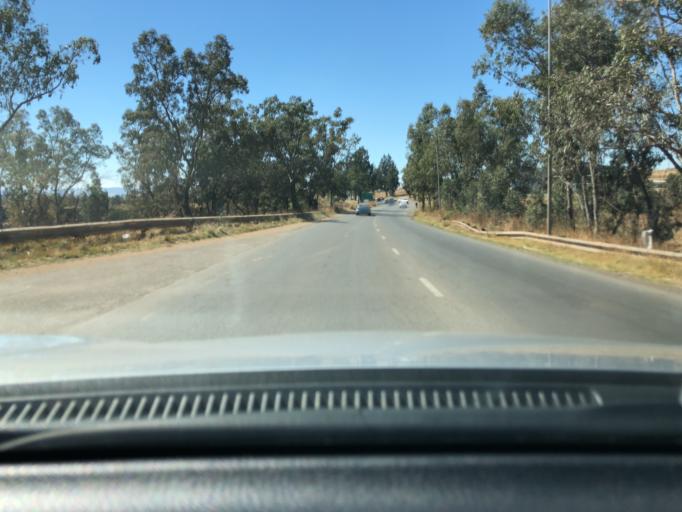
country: ZA
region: KwaZulu-Natal
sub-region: Amajuba District Municipality
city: Newcastle
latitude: -27.7618
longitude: 29.9569
